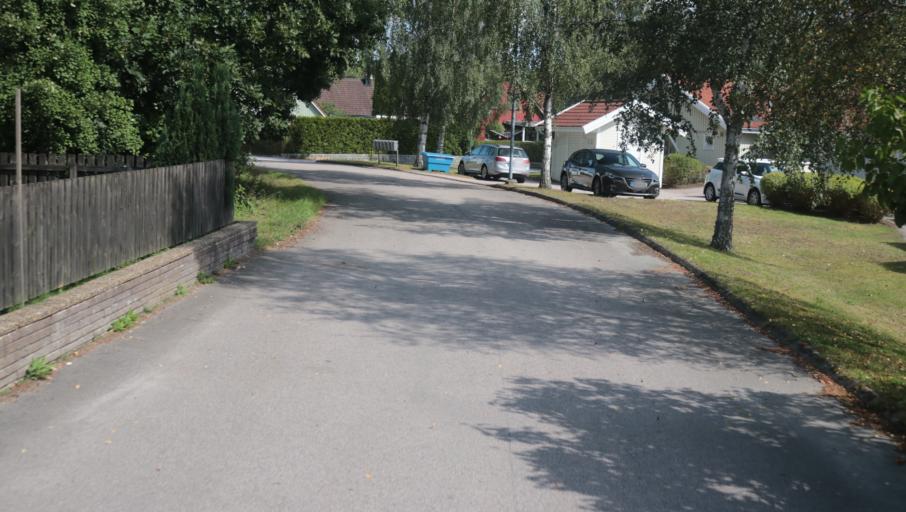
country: SE
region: Blekinge
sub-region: Karlshamns Kommun
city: Karlshamn
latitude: 56.1964
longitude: 14.8438
